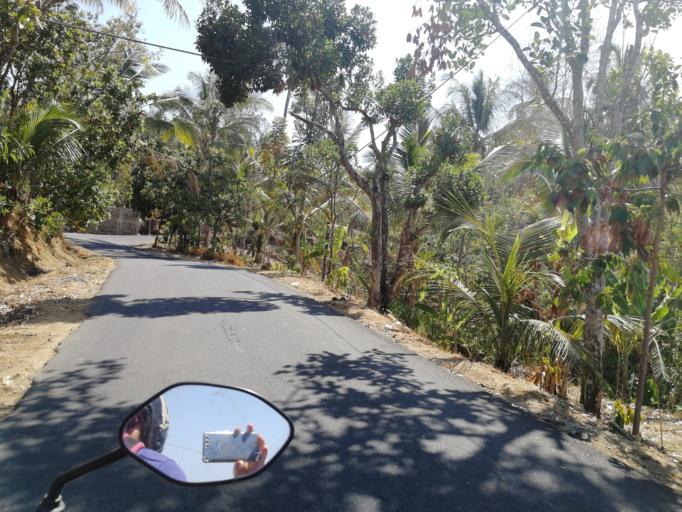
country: ID
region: Bali
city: Banjar Kedisan
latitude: -8.1400
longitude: 115.3162
